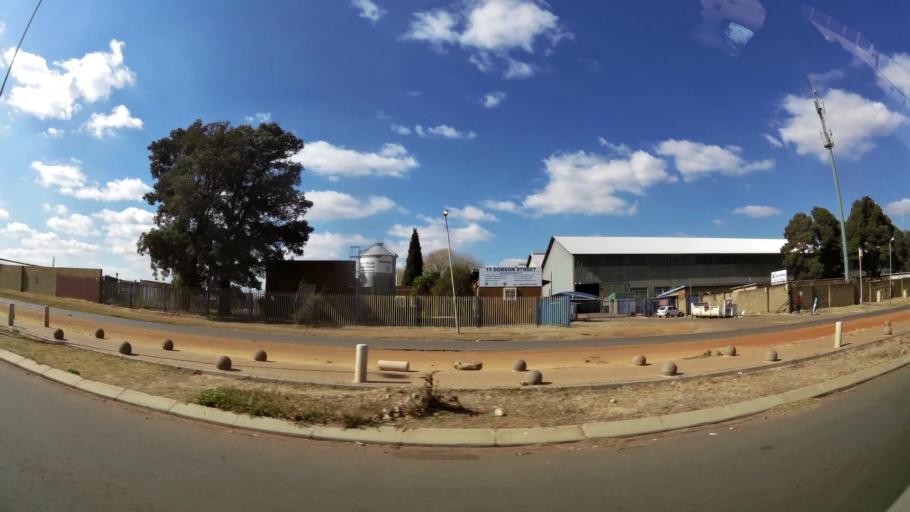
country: ZA
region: Gauteng
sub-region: West Rand District Municipality
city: Krugersdorp
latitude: -26.1459
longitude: 27.7906
